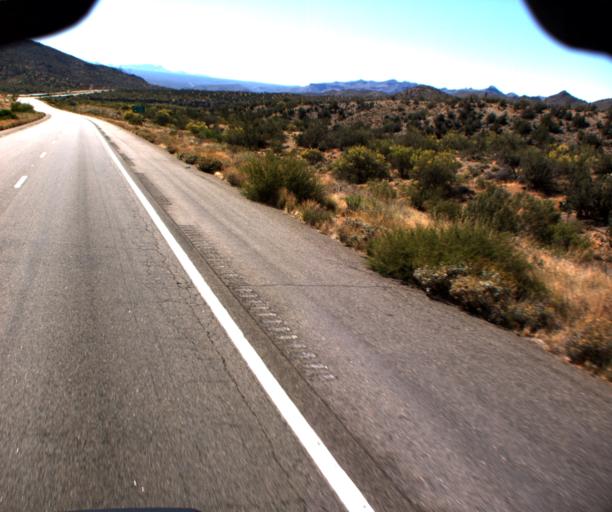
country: US
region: Arizona
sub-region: Yavapai County
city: Bagdad
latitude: 34.4303
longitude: -113.2511
